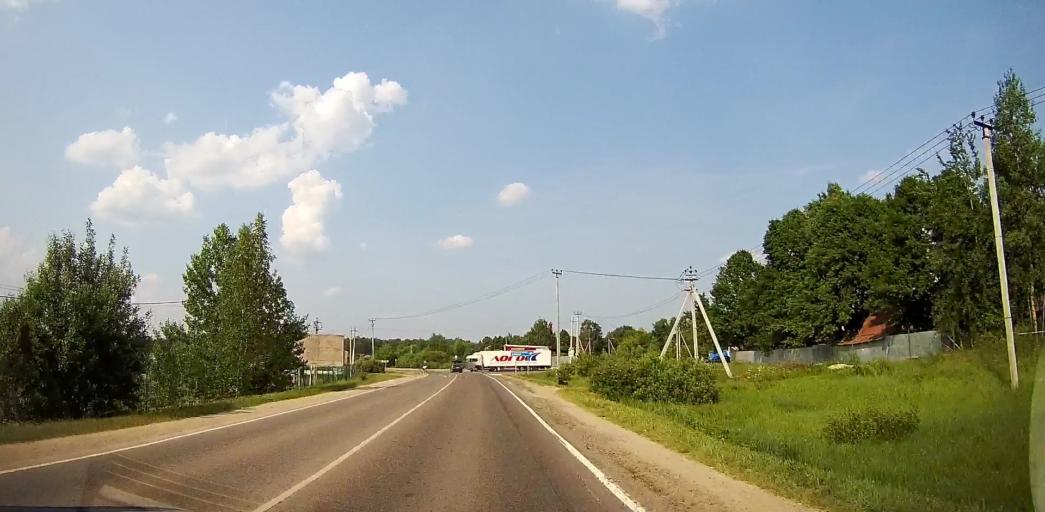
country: RU
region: Moskovskaya
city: Mikhnevo
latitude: 55.1582
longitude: 37.9614
